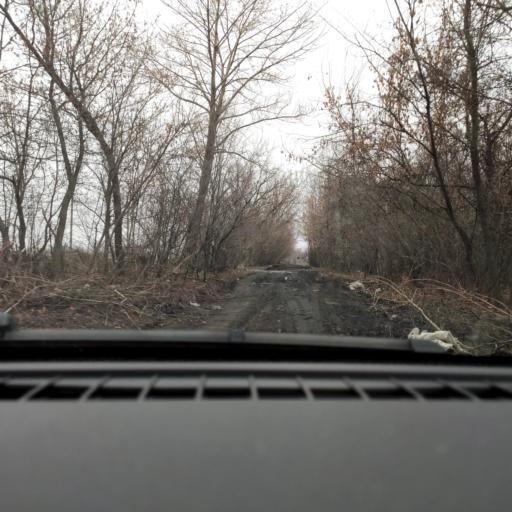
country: RU
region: Voronezj
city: Maslovka
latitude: 51.6086
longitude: 39.2721
